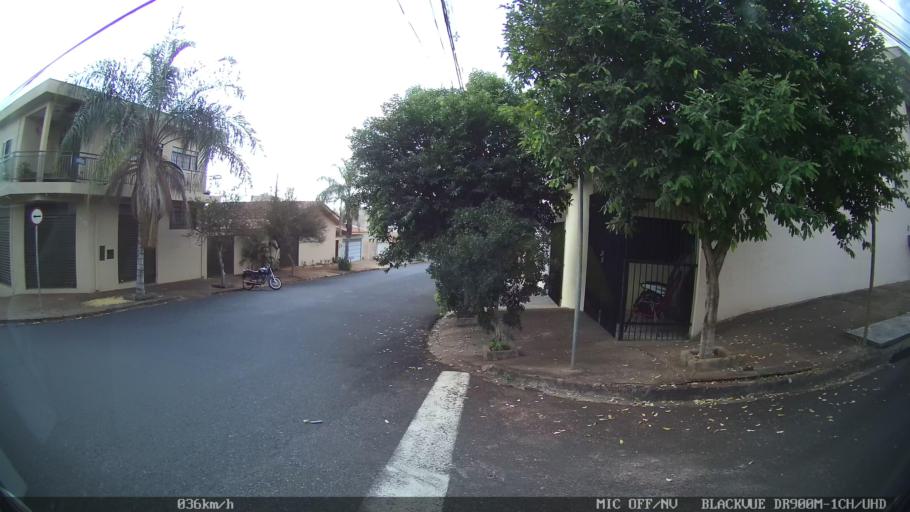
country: BR
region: Sao Paulo
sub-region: Ribeirao Preto
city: Ribeirao Preto
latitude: -21.1809
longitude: -47.8391
